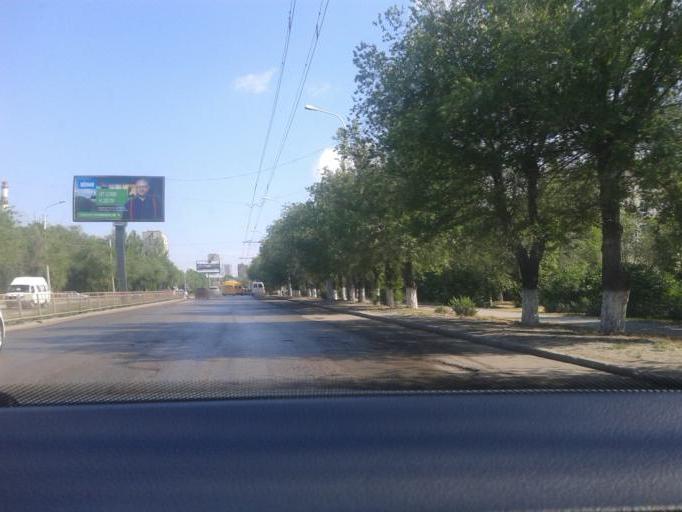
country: RU
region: Volgograd
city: Volgograd
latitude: 48.6100
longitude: 44.4225
